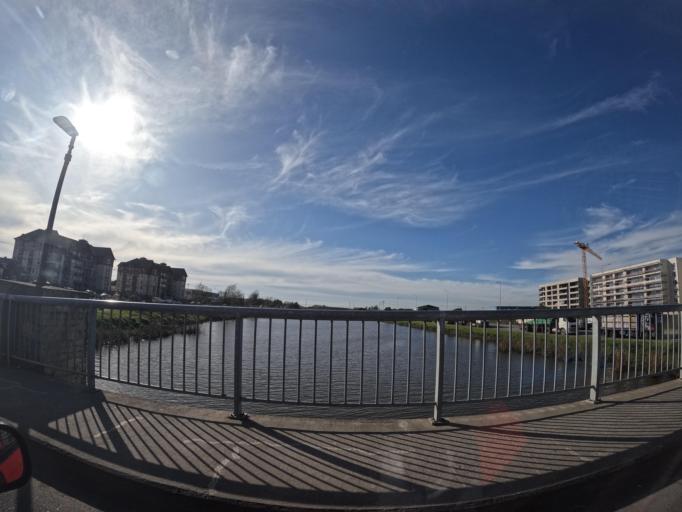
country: CL
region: Biobio
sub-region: Provincia de Concepcion
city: Talcahuano
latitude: -36.7695
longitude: -73.0751
